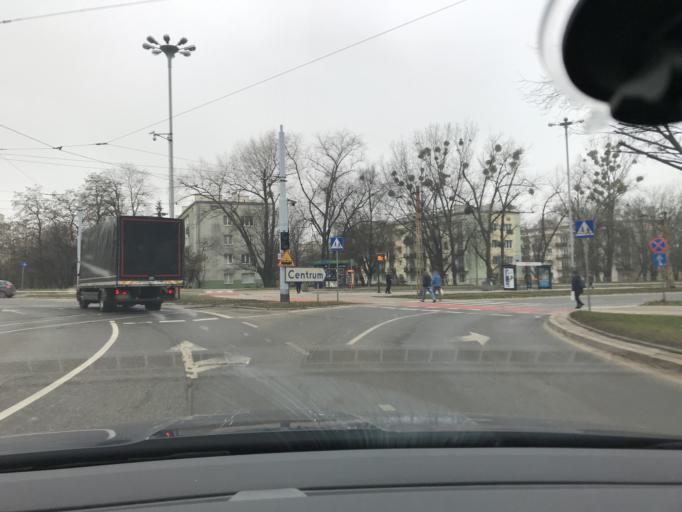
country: PL
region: Lodz Voivodeship
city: Lodz
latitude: 51.7319
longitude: 19.4535
